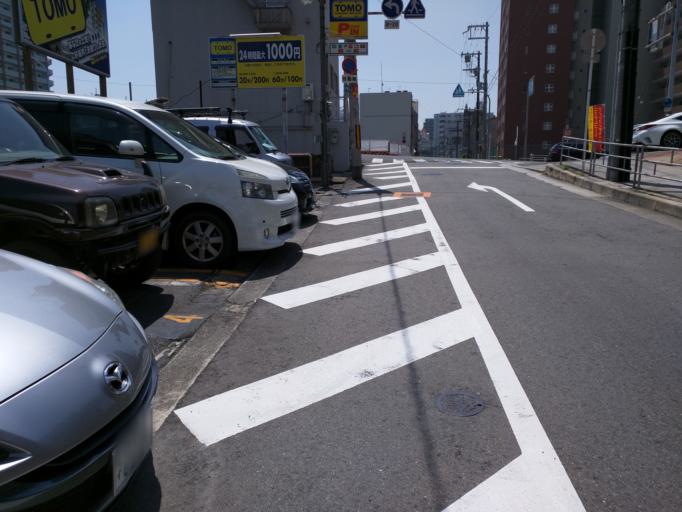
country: JP
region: Osaka
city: Osaka-shi
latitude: 34.6834
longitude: 135.4828
